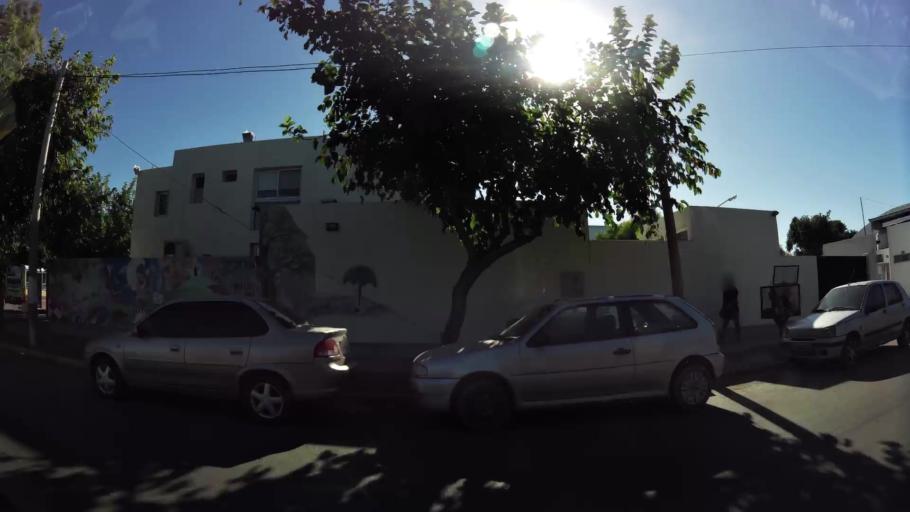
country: AR
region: San Juan
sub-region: Departamento de Santa Lucia
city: Santa Lucia
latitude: -31.5378
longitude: -68.5099
